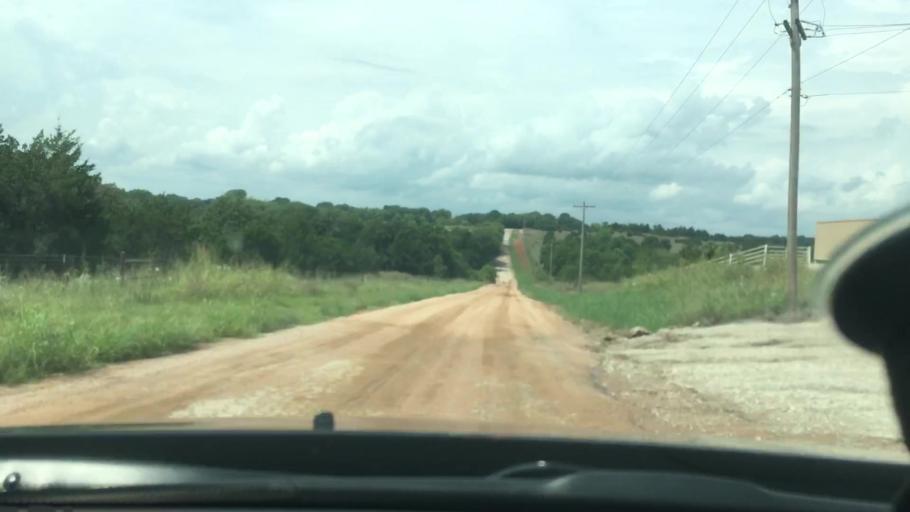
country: US
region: Oklahoma
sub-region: Carter County
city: Dickson
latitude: 34.2454
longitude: -96.9206
